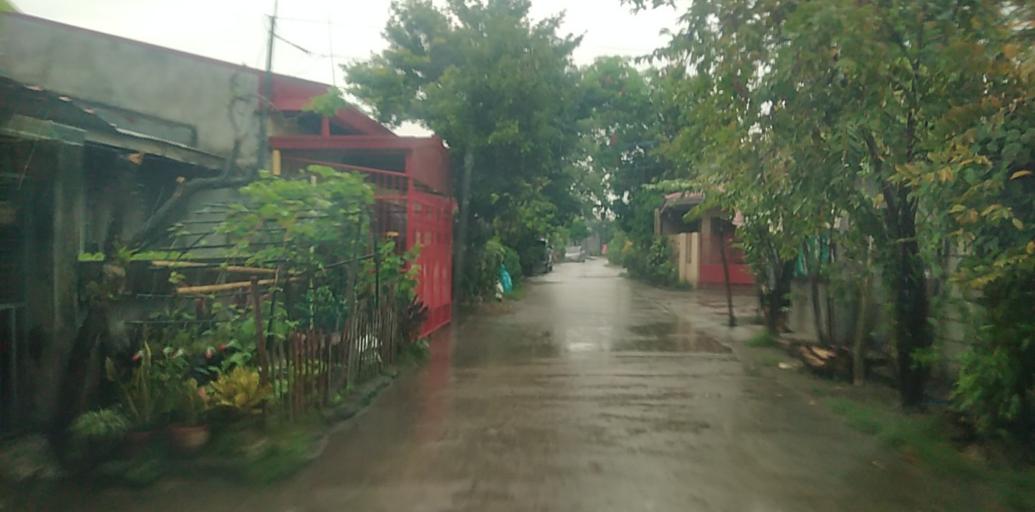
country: PH
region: Central Luzon
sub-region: Province of Pampanga
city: Arenas
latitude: 15.1710
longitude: 120.6826
